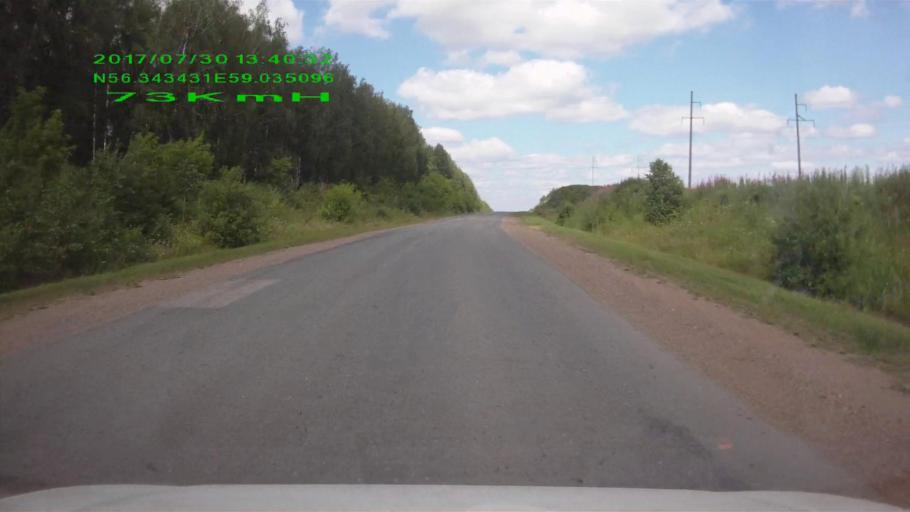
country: RU
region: Sverdlovsk
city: Mikhaylovsk
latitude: 56.3438
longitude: 59.0351
